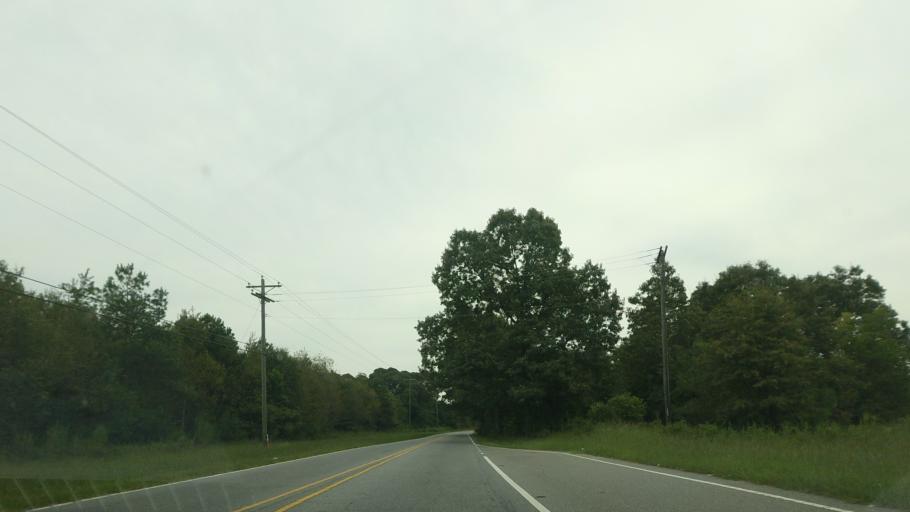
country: US
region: Georgia
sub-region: Houston County
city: Robins Air Force Base
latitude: 32.5924
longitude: -83.6088
